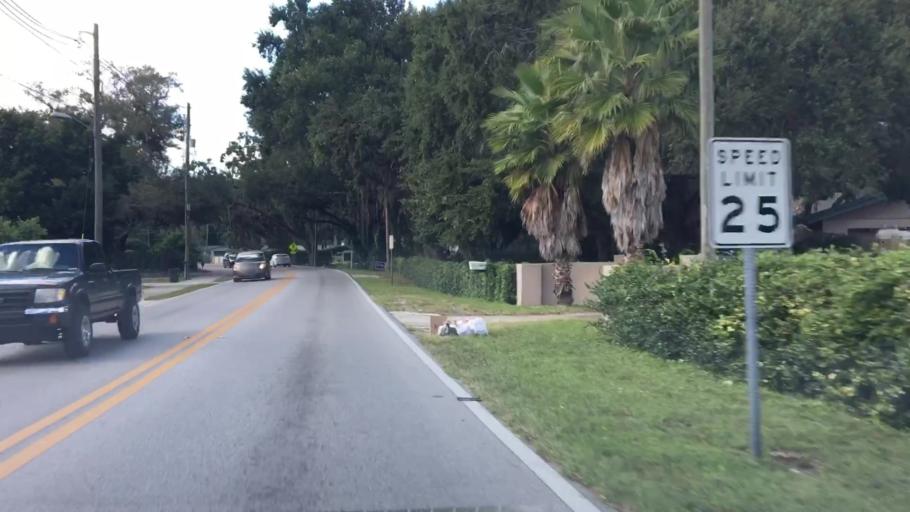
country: US
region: Florida
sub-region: Orange County
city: Pine Castle
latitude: 28.4846
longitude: -81.3503
